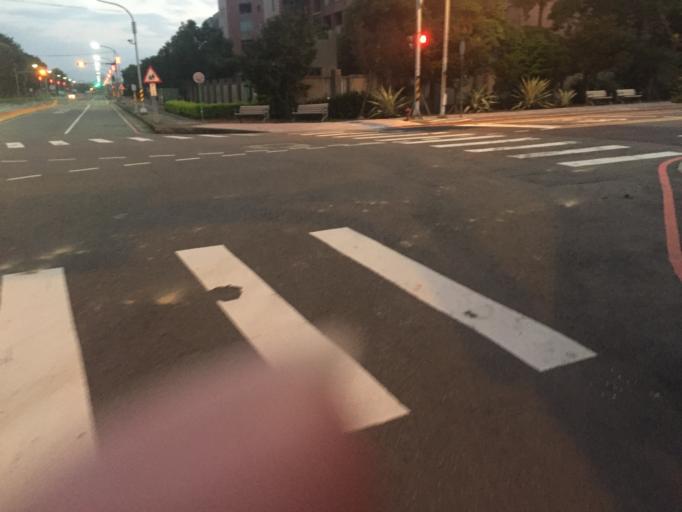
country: TW
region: Taiwan
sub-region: Taoyuan
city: Taoyuan
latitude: 24.9776
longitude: 121.3145
